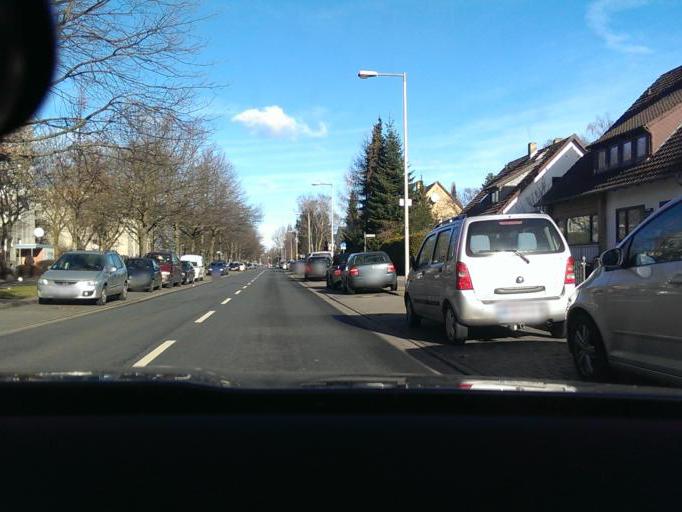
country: DE
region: Lower Saxony
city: Langenhagen
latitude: 52.4121
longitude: 9.7815
